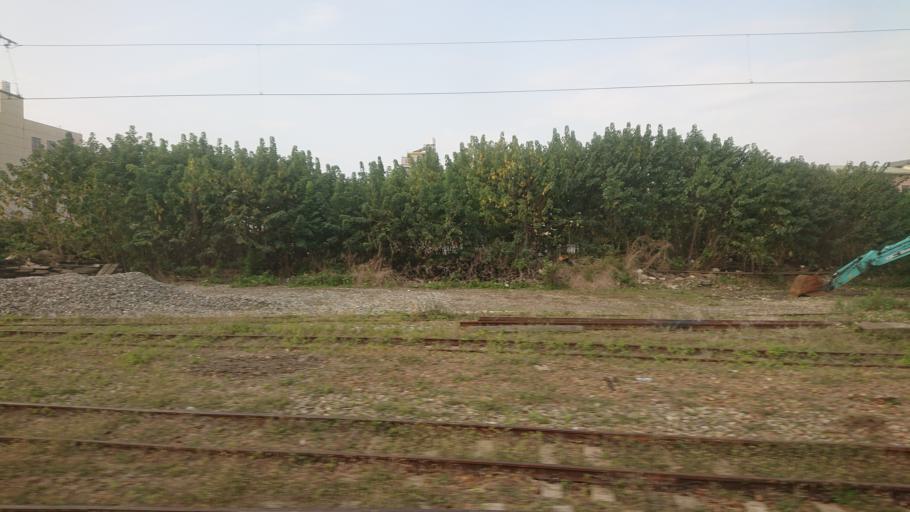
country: TW
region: Taiwan
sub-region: Nantou
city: Nantou
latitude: 23.8561
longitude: 120.5923
